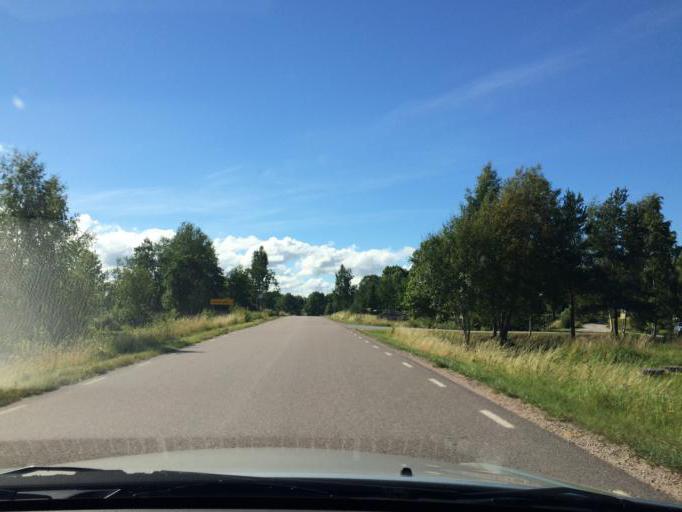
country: SE
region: Soedermanland
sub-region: Eskilstuna Kommun
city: Torshalla
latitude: 59.5277
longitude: 16.4415
